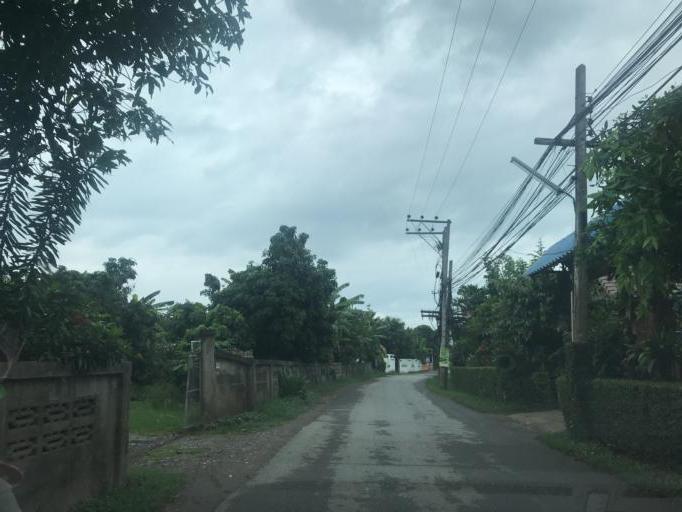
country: TH
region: Chiang Mai
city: Saraphi
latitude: 18.6984
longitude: 99.0222
